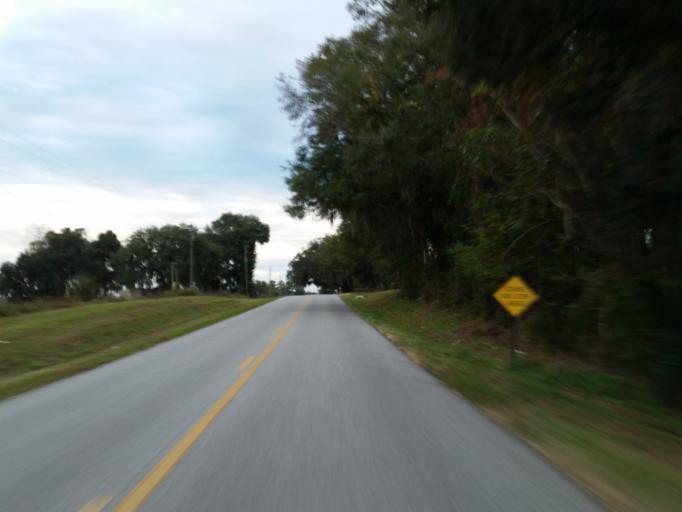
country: US
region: Florida
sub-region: Hamilton County
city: Jasper
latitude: 30.5393
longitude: -83.1026
